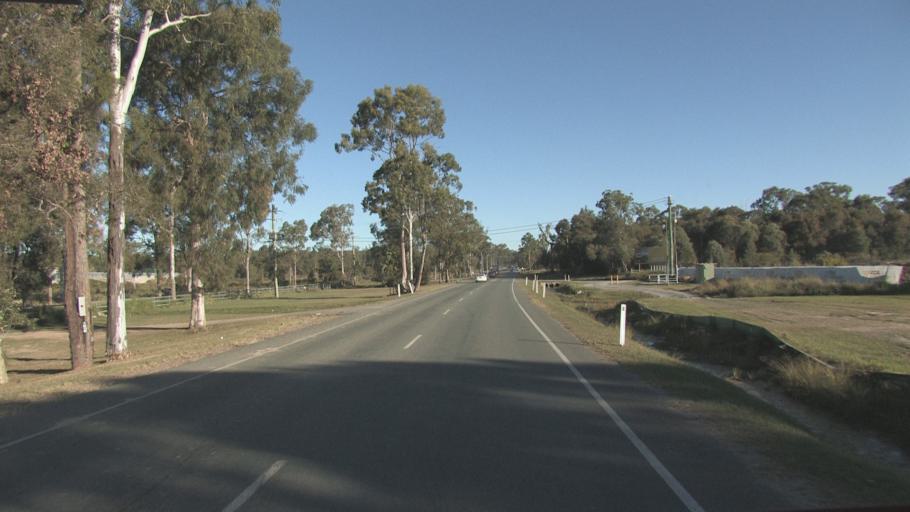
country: AU
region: Queensland
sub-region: Logan
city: Logan Reserve
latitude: -27.7146
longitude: 153.0927
